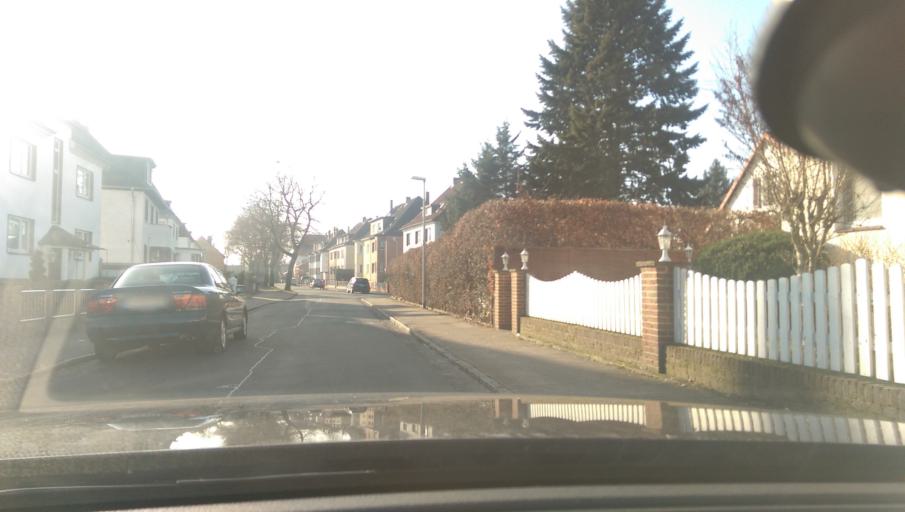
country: DE
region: Lower Saxony
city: Langenhagen
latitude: 52.4200
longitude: 9.6983
